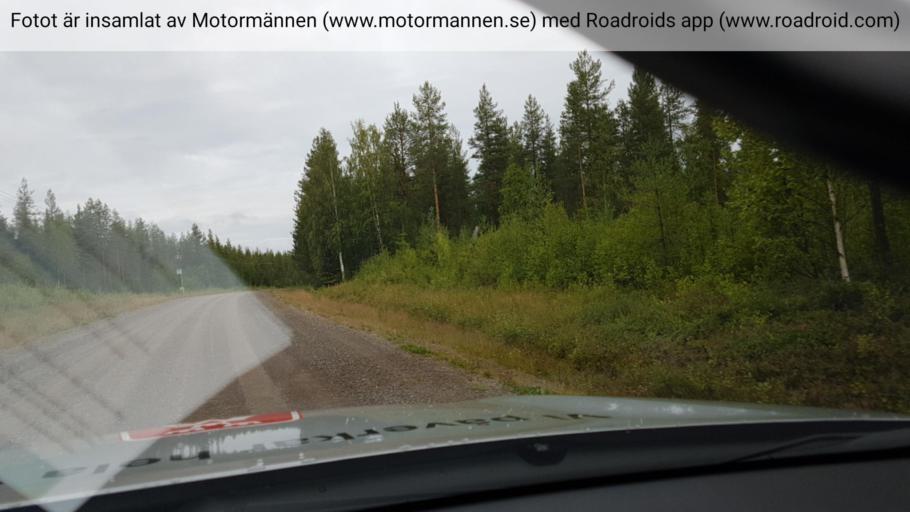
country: SE
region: Norrbotten
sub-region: Alvsbyns Kommun
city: AElvsbyn
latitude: 66.0318
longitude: 20.9960
